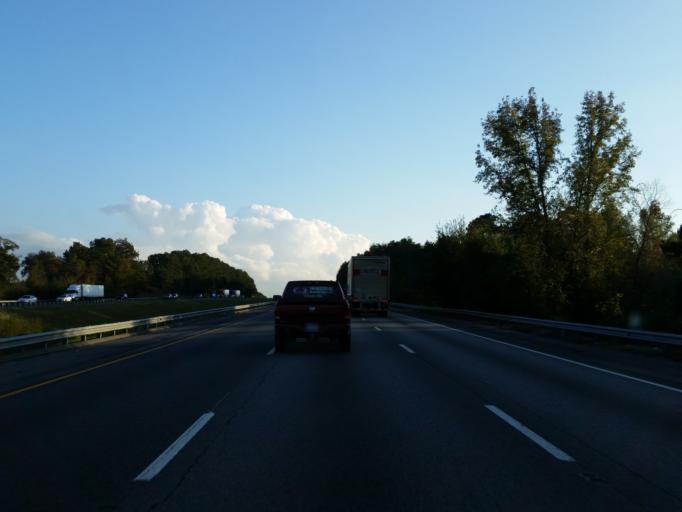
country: US
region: Georgia
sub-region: Houston County
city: Perry
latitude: 32.5292
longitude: -83.7438
